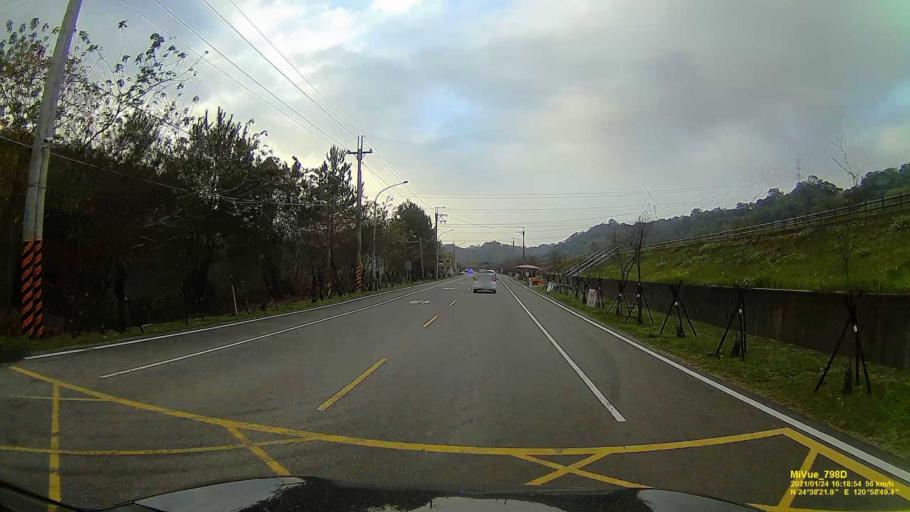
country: TW
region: Taiwan
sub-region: Hsinchu
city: Hsinchu
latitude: 24.6396
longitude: 120.9802
